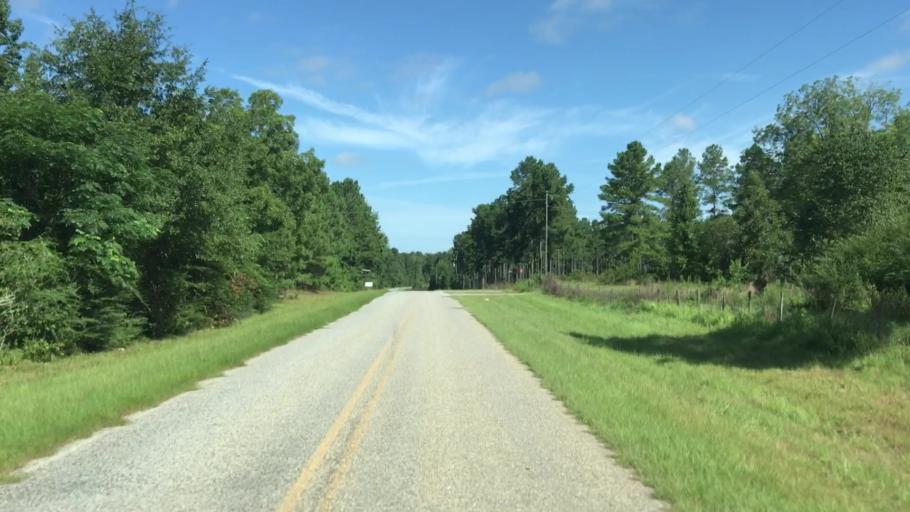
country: US
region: Georgia
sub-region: Jefferson County
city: Wadley
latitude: 32.8077
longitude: -82.3720
